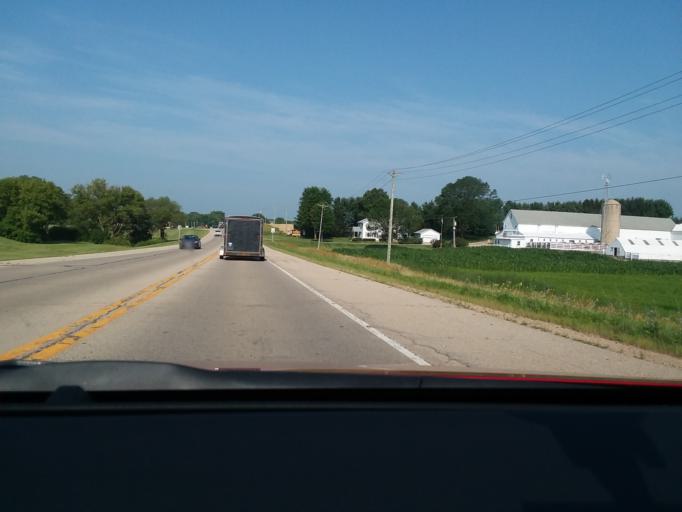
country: US
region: Wisconsin
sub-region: Dane County
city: Waunakee
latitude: 43.1921
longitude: -89.4395
